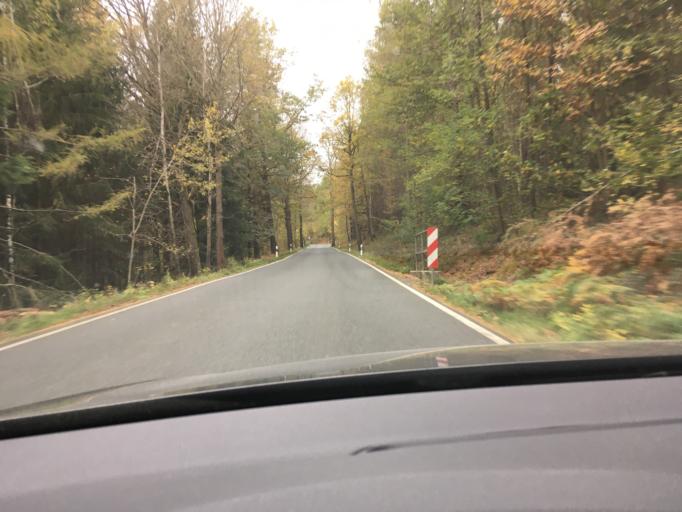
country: DE
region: Saxony
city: Reinhardtsgrimma
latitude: 50.8947
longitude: 13.7843
